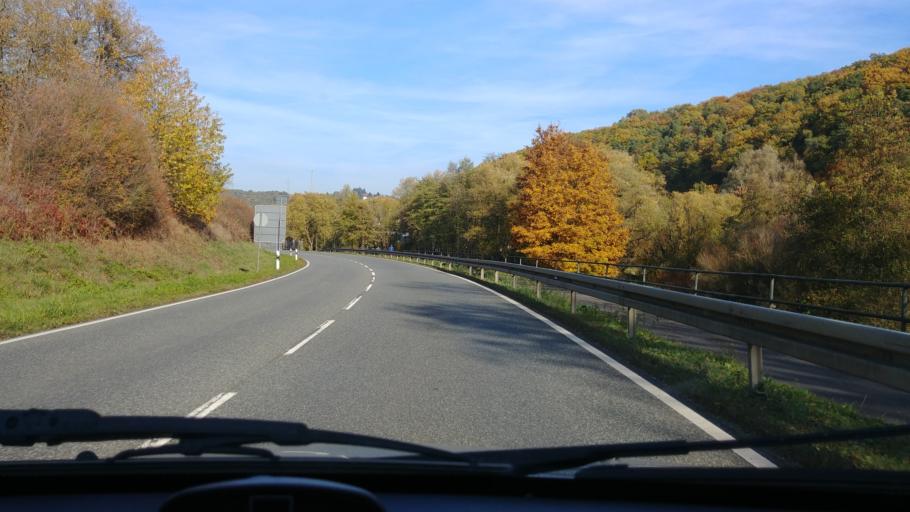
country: DE
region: Hesse
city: Burg Hohenstein
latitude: 50.2349
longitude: 8.0598
